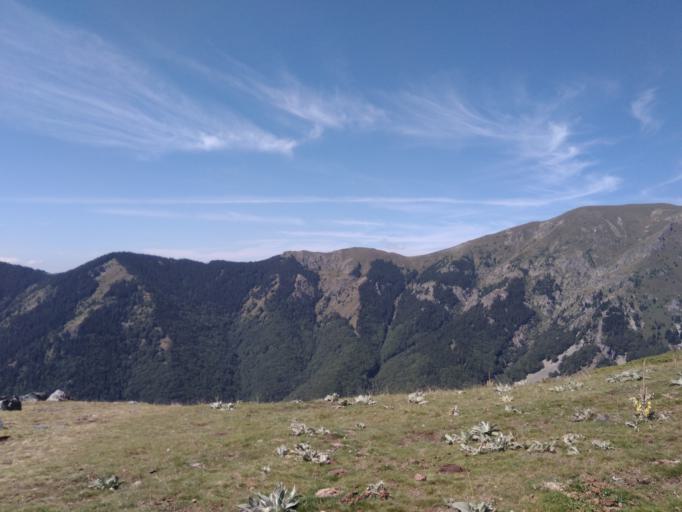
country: BG
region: Plovdiv
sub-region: Obshtina Karlovo
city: Karlovo
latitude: 42.7098
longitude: 24.8140
